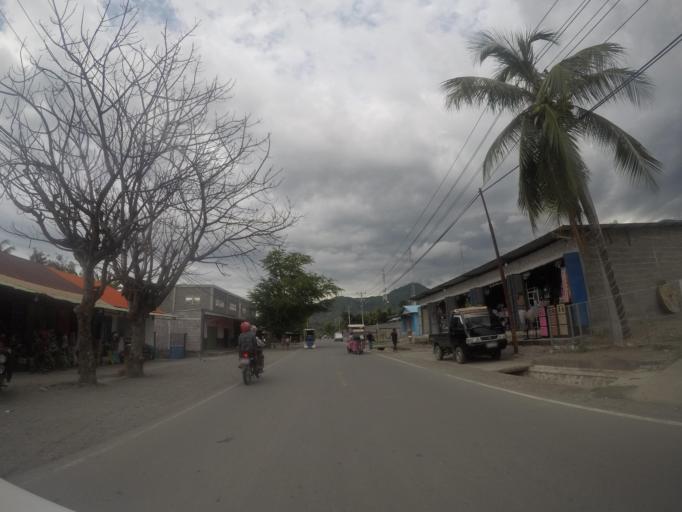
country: TL
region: Liquica
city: Liquica
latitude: -8.5897
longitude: 125.3412
